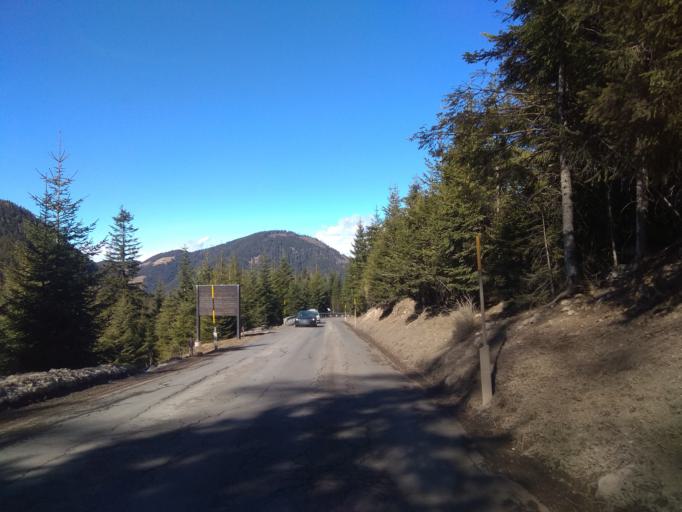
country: IT
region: Trentino-Alto Adige
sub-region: Bolzano
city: Nova Levante
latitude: 46.4133
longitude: 11.5646
